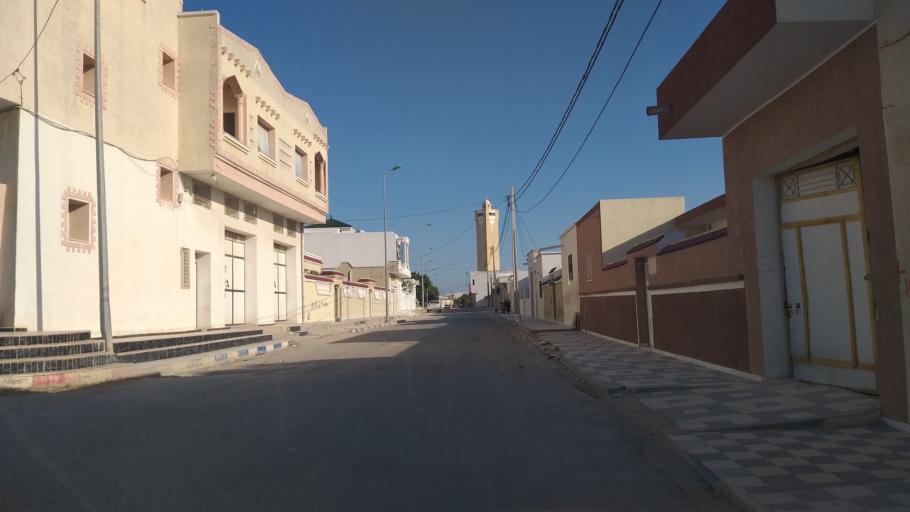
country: TN
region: Al Mahdiyah
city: El Jem
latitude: 35.2896
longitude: 10.7073
